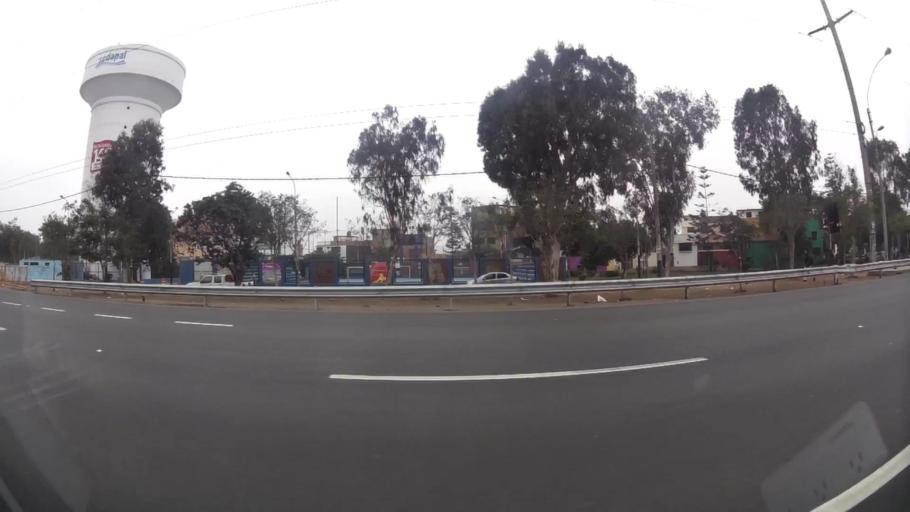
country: PE
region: Lima
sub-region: Lima
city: Surco
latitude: -12.1539
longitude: -76.9839
